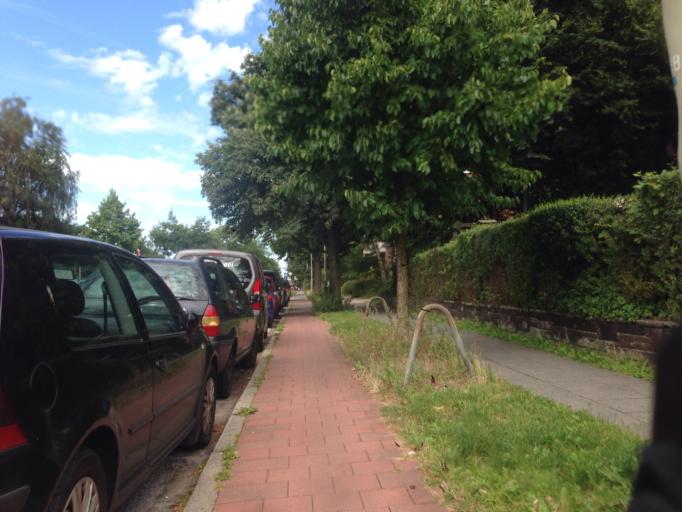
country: DE
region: Hamburg
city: Barmbek-Nord
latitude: 53.5921
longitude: 10.0384
